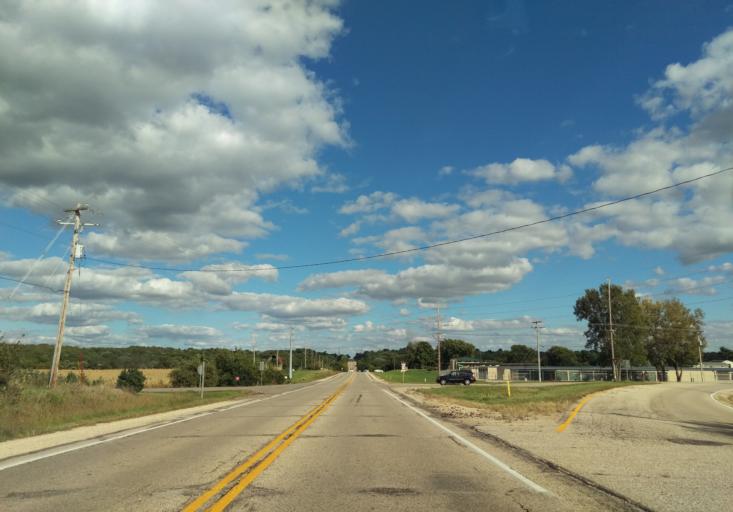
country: US
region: Wisconsin
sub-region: Rock County
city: Janesville
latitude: 42.7301
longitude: -89.0680
